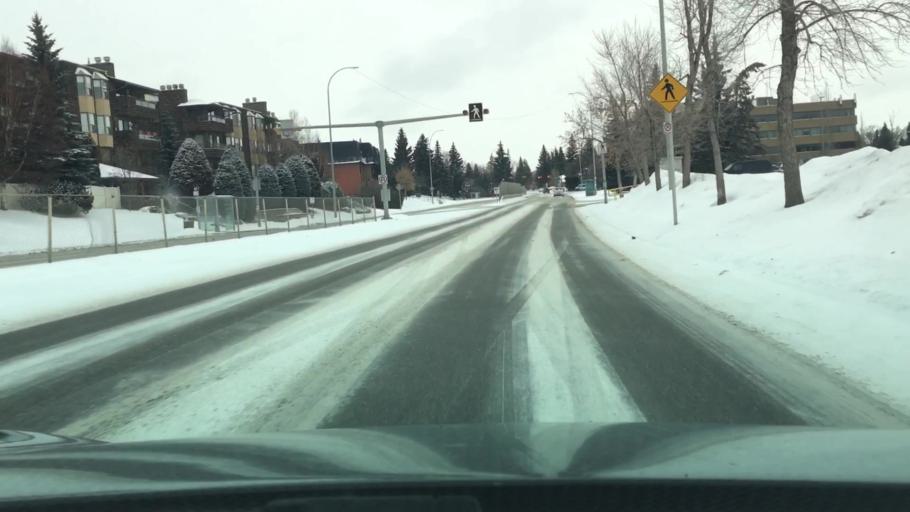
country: CA
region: Alberta
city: Calgary
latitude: 51.0857
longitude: -114.1589
